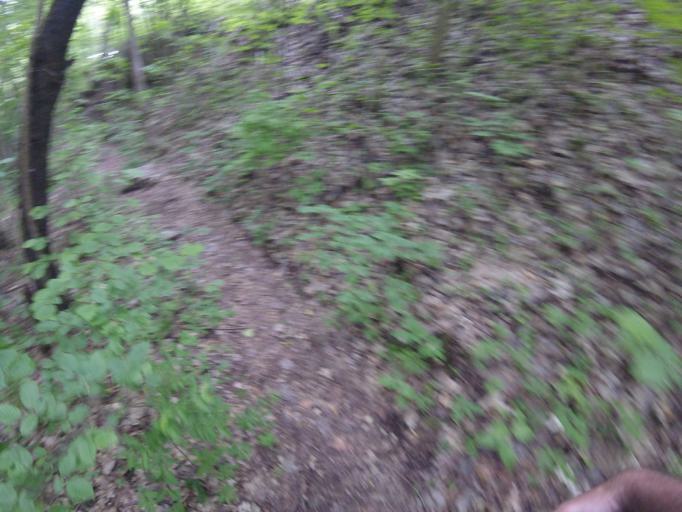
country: SK
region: Kosicky
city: Medzev
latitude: 48.6423
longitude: 20.8480
